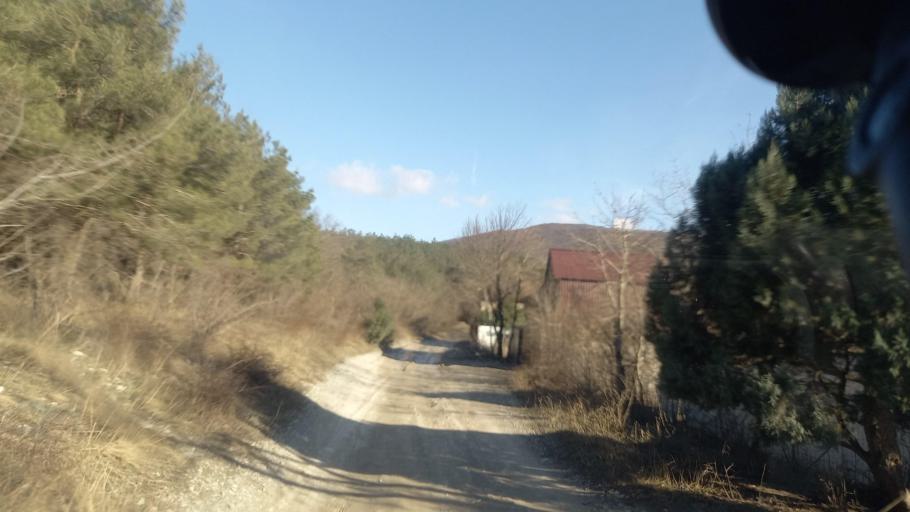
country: RU
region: Krasnodarskiy
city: Kabardinka
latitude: 44.6297
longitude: 37.9260
